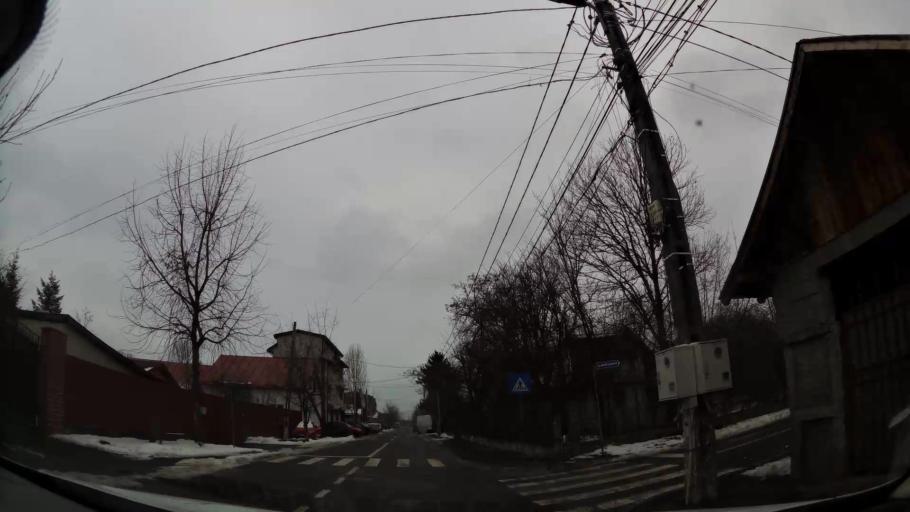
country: RO
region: Ilfov
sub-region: Comuna Otopeni
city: Otopeni
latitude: 44.5570
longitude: 26.0742
